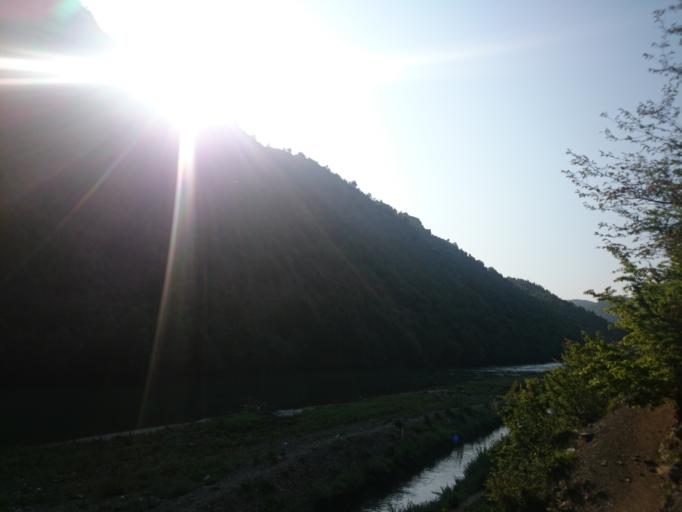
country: AL
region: Diber
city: Peshkopi
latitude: 41.6477
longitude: 20.3945
